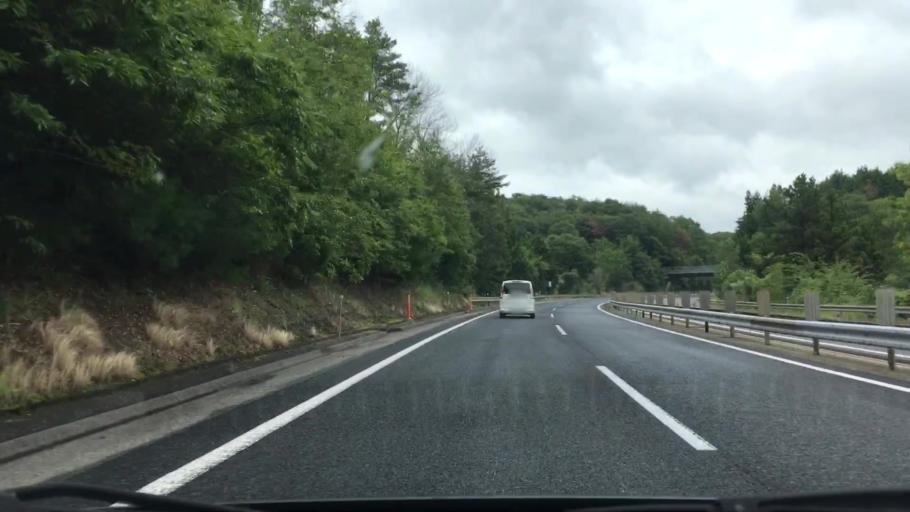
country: JP
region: Hiroshima
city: Miyoshi
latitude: 34.7458
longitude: 132.7230
